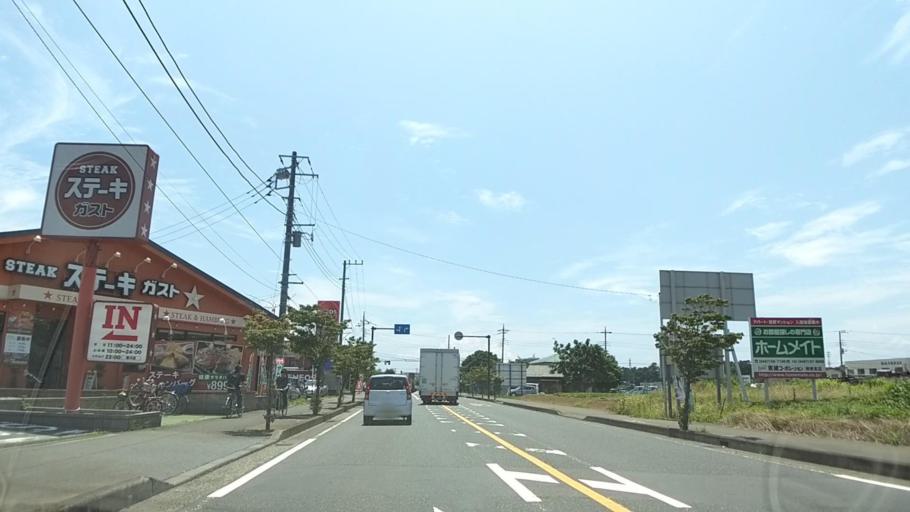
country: JP
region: Kanagawa
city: Chigasaki
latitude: 35.3776
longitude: 139.3849
